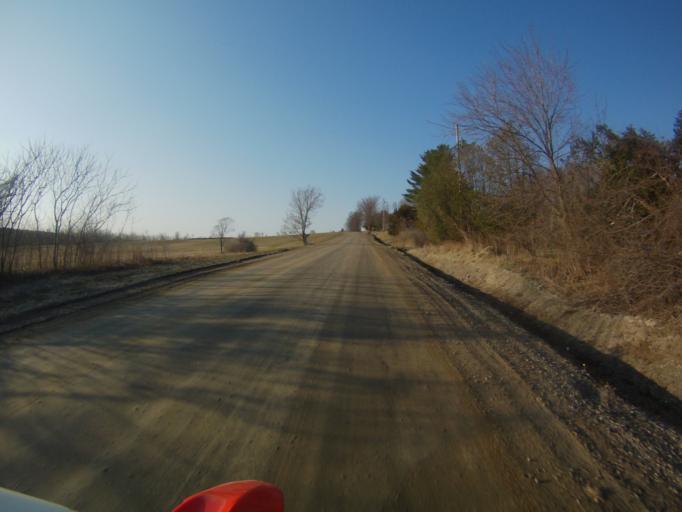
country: US
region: Vermont
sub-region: Addison County
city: Bristol
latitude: 44.1031
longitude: -73.0883
